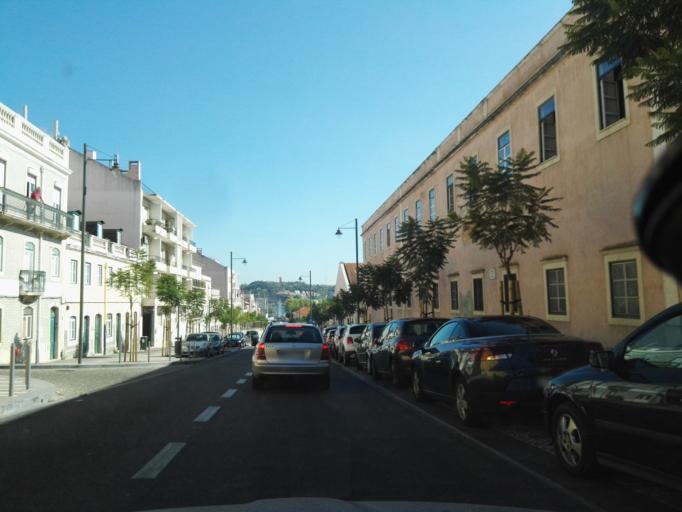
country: PT
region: Lisbon
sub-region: Oeiras
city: Alges
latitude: 38.6999
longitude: -9.1999
